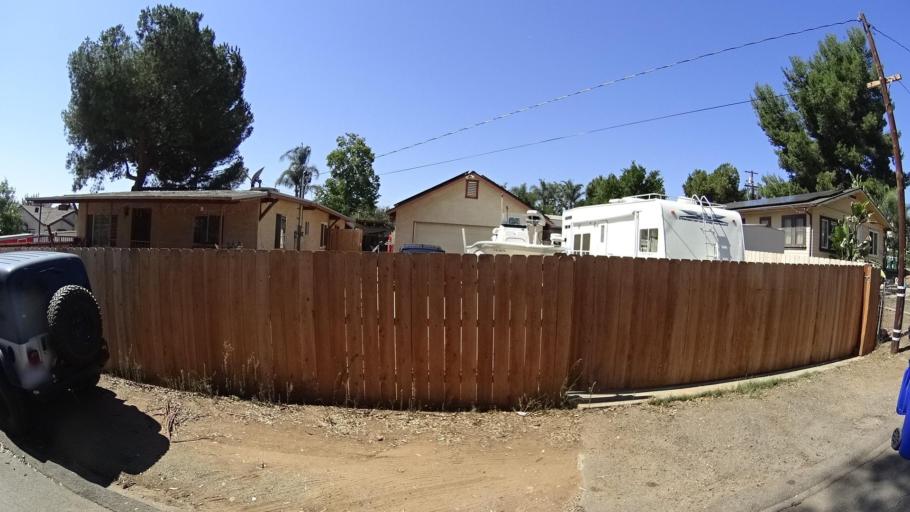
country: US
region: California
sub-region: San Diego County
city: Crest
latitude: 32.8088
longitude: -116.8653
